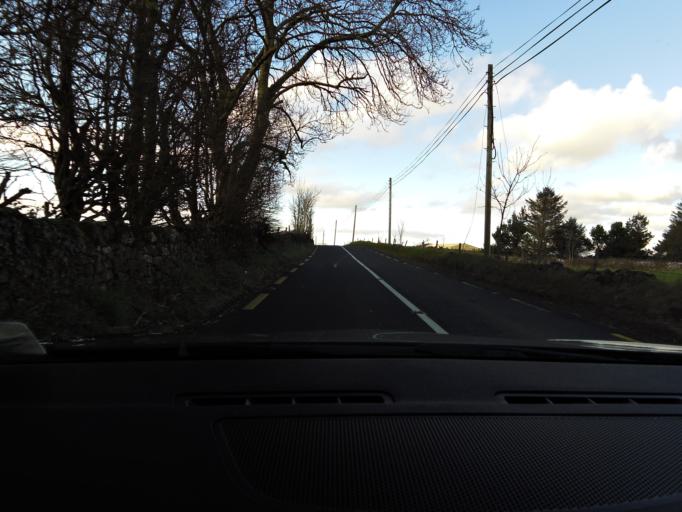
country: IE
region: Connaught
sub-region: Roscommon
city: Roscommon
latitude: 53.6836
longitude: -8.1966
